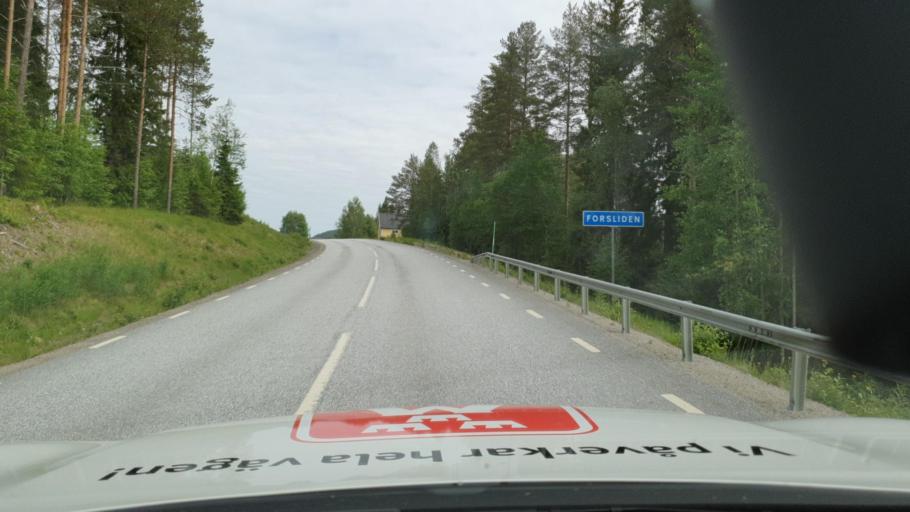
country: SE
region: Vaesterbotten
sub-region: Umea Kommun
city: Ersmark
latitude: 64.2931
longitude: 20.2244
